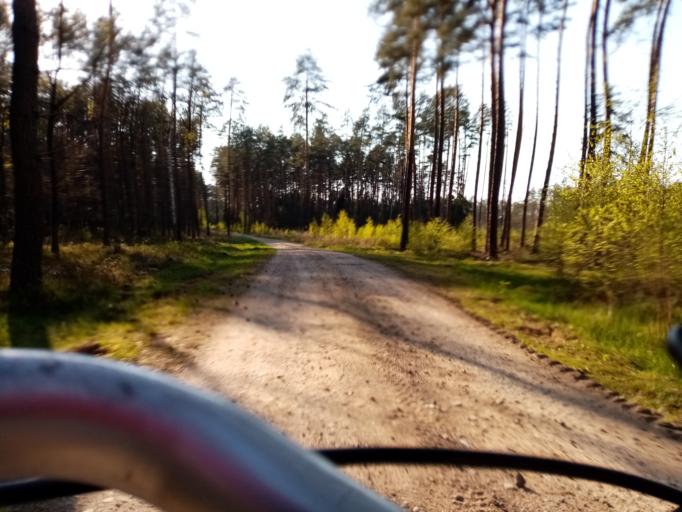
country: PL
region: Kujawsko-Pomorskie
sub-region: Powiat brodnicki
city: Gorzno
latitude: 53.1591
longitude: 19.6897
